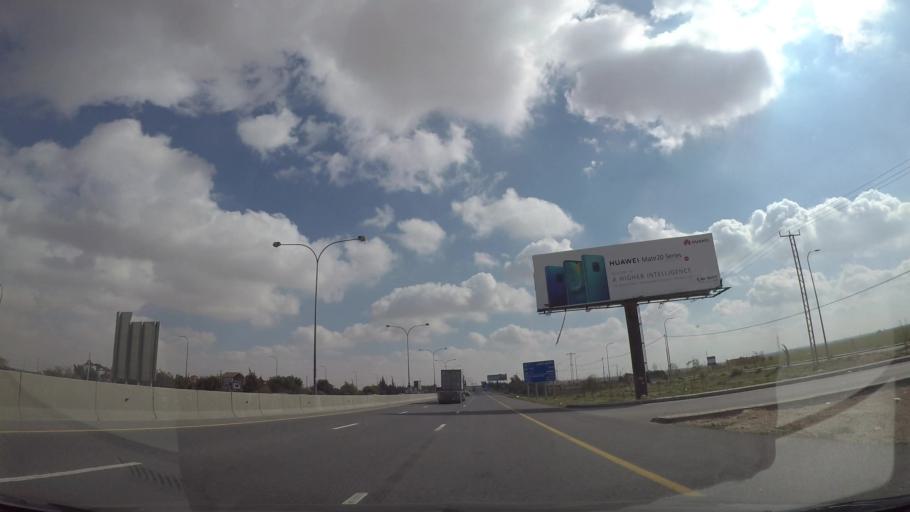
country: JO
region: Amman
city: Al Jizah
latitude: 31.7298
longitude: 35.9450
